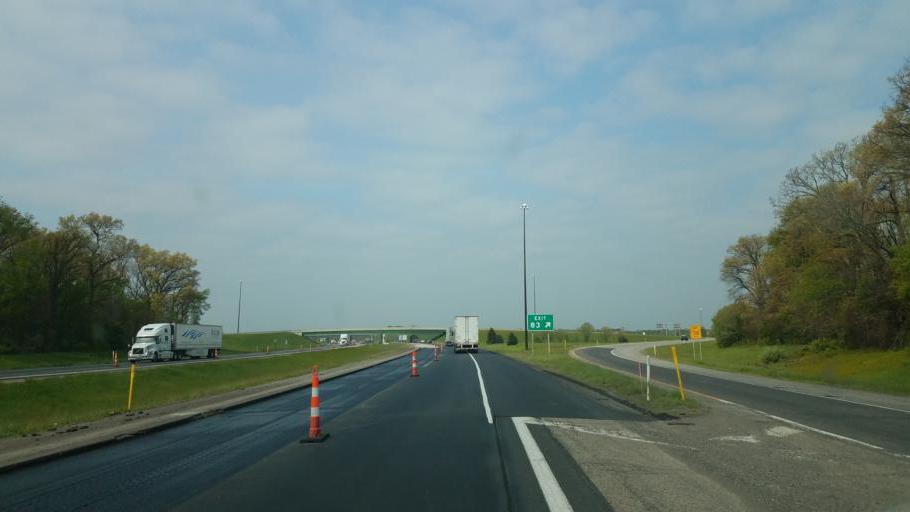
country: US
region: Indiana
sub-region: Saint Joseph County
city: Granger
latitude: 41.7332
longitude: -86.1374
